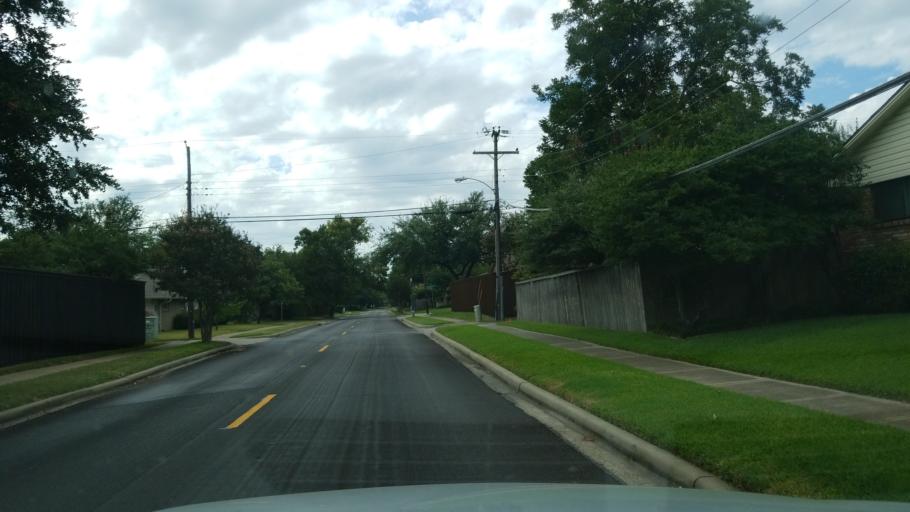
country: US
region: Texas
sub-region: Dallas County
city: Richardson
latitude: 32.9694
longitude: -96.7724
